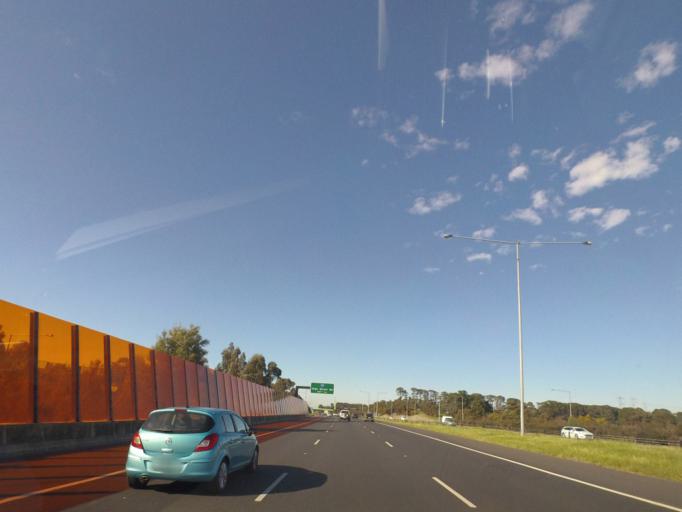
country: AU
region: Victoria
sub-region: Knox
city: Wantirna
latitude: -37.8622
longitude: 145.2118
